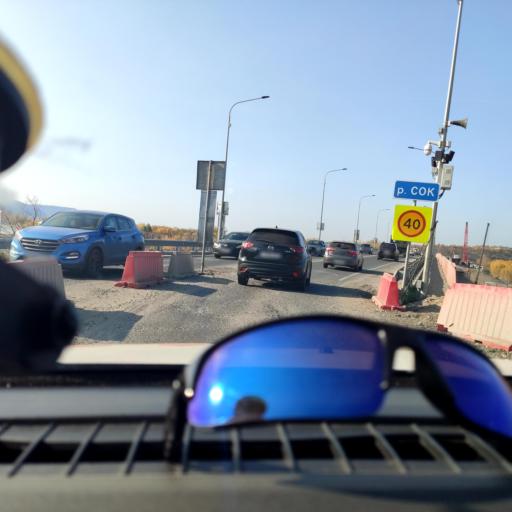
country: RU
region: Samara
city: Volzhskiy
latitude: 53.4110
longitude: 50.1389
